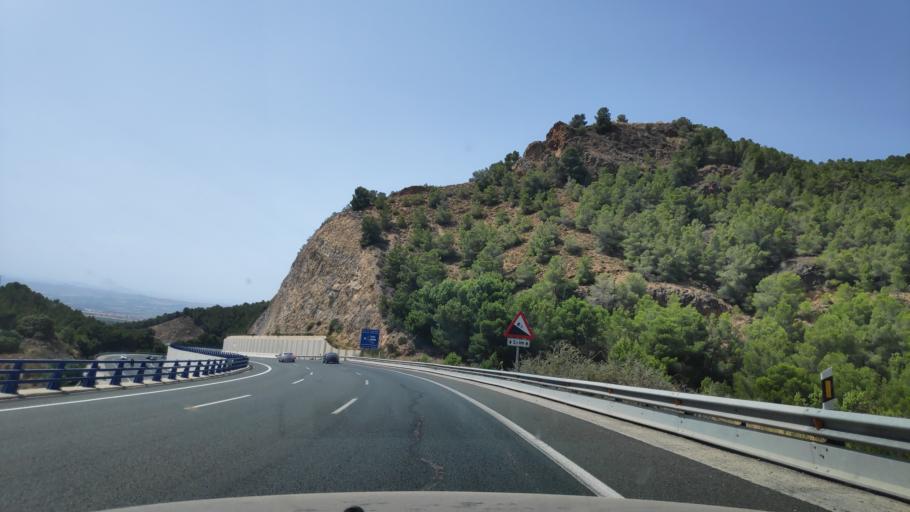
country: ES
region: Murcia
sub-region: Murcia
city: Murcia
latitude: 37.9048
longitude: -1.1462
